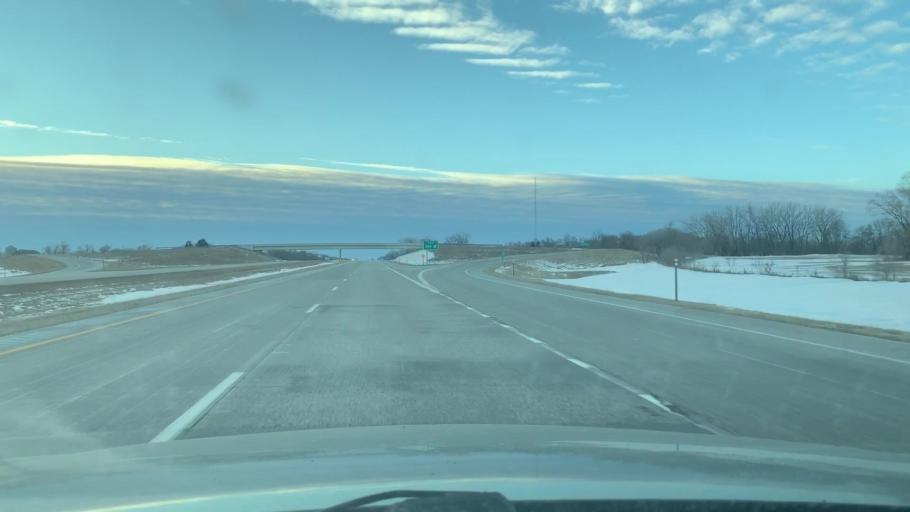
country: US
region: North Dakota
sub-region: Cass County
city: Casselton
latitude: 46.8762
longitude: -97.4246
